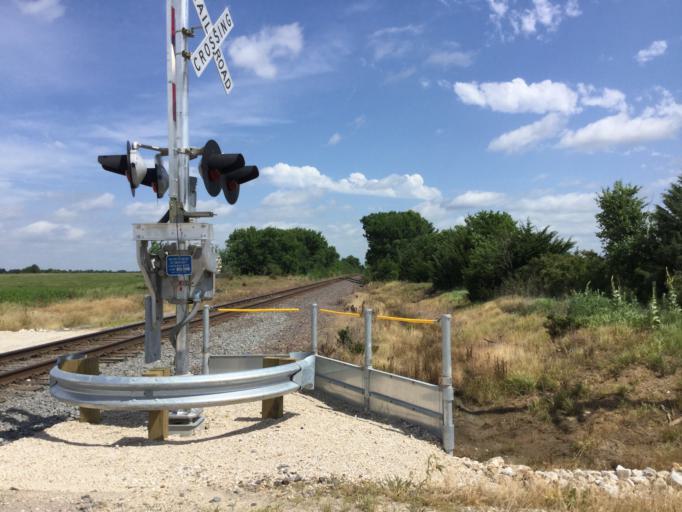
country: US
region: Kansas
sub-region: Woodson County
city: Yates Center
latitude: 37.9082
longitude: -95.6959
